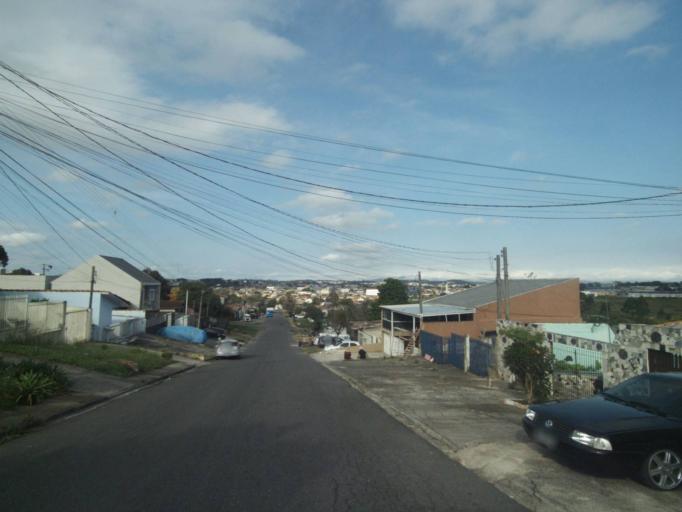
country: BR
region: Parana
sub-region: Pinhais
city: Pinhais
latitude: -25.4064
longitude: -49.1985
